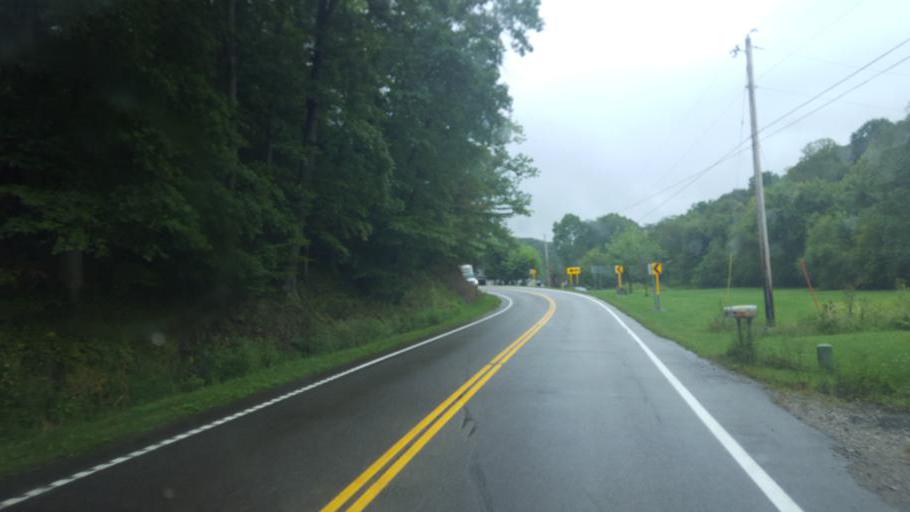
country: US
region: Ohio
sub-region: Jackson County
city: Oak Hill
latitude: 38.8494
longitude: -82.6312
